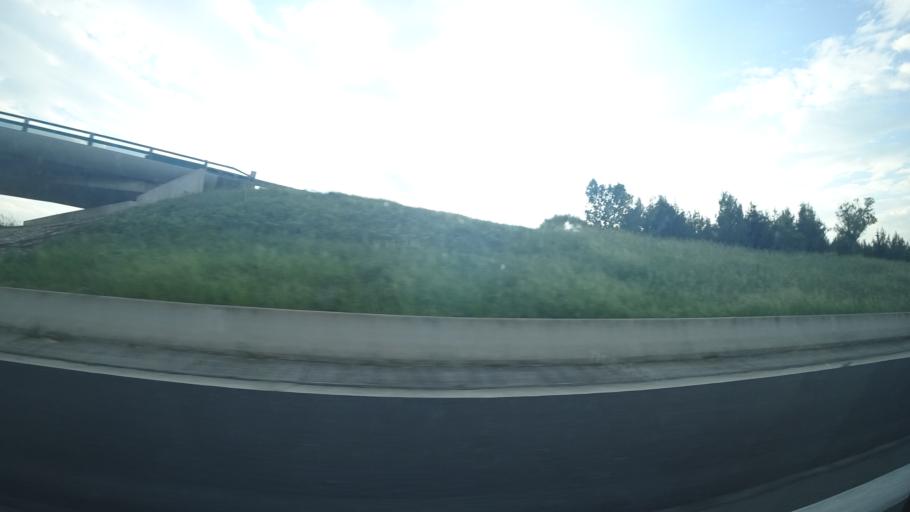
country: FR
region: Languedoc-Roussillon
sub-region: Departement de l'Herault
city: Aspiran
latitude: 43.5725
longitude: 3.4643
